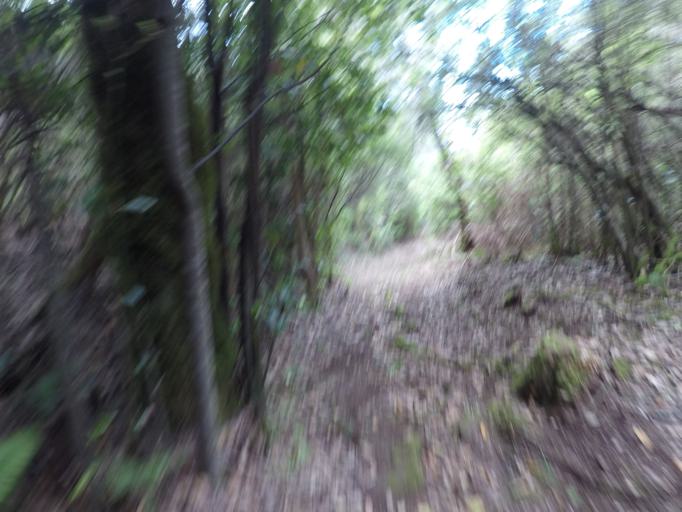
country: PT
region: Madeira
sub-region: Camara de Lobos
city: Curral das Freiras
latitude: 32.7753
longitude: -16.9809
